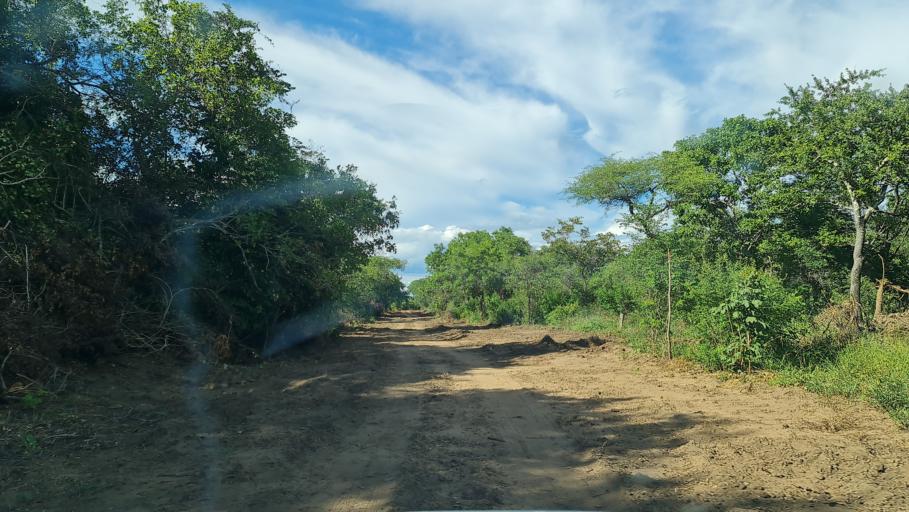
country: MZ
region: Nampula
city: Antonio Enes
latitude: -15.5165
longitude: 40.1301
